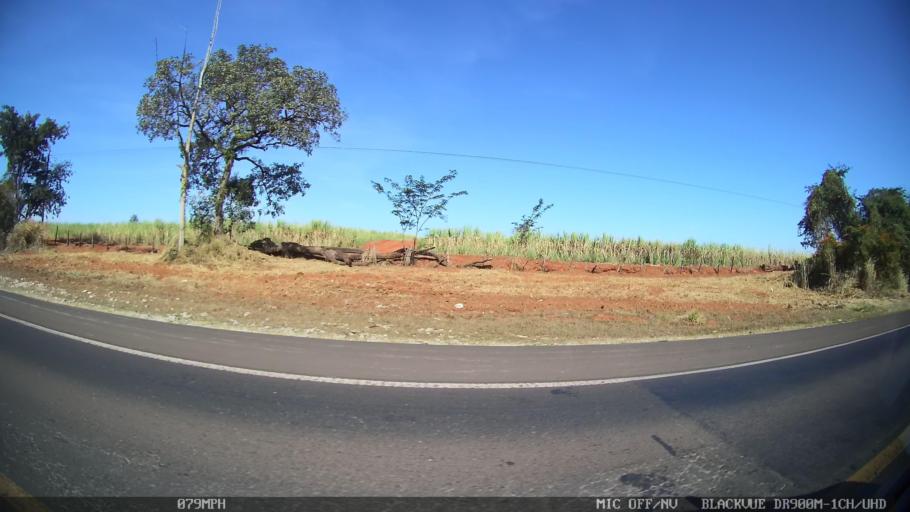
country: BR
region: Sao Paulo
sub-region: Barretos
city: Barretos
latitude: -20.5912
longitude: -48.7088
